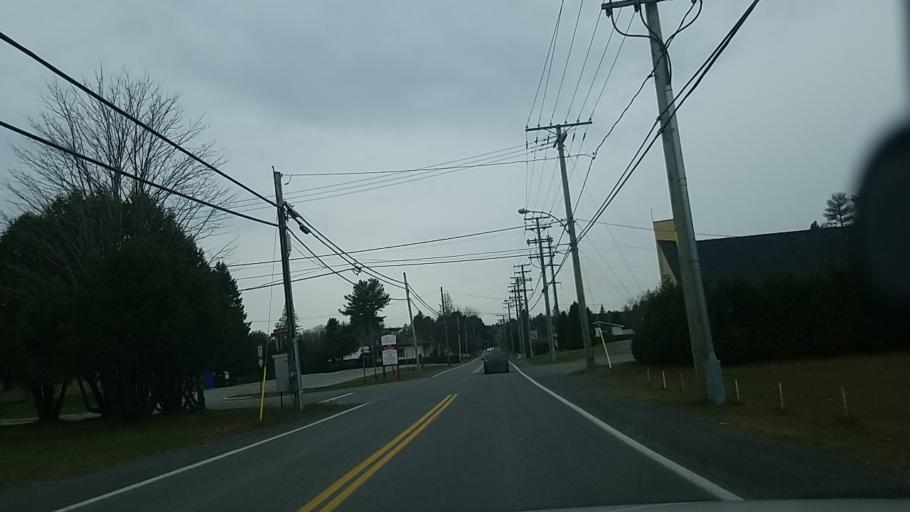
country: CA
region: Quebec
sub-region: Laurentides
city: Saint-Colomban
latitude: 45.7855
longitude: -74.0809
